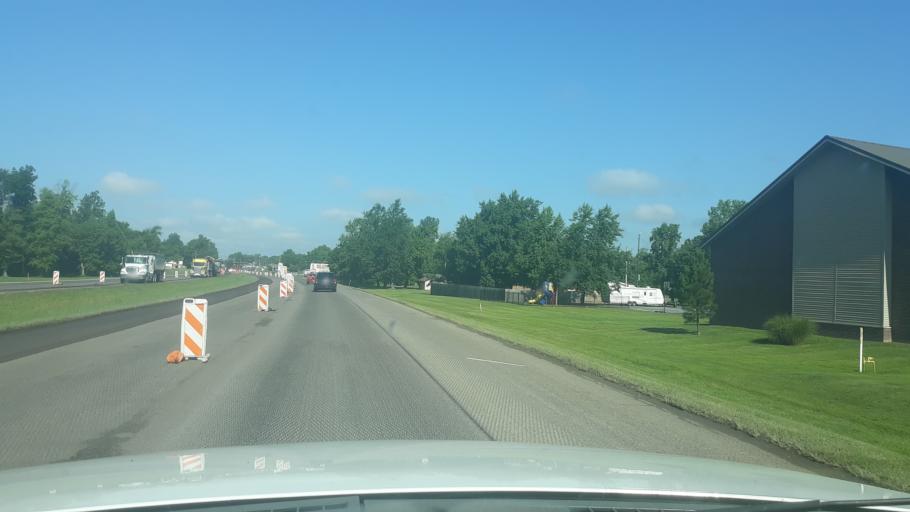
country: US
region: Illinois
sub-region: Williamson County
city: Marion
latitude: 37.7397
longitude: -88.9049
